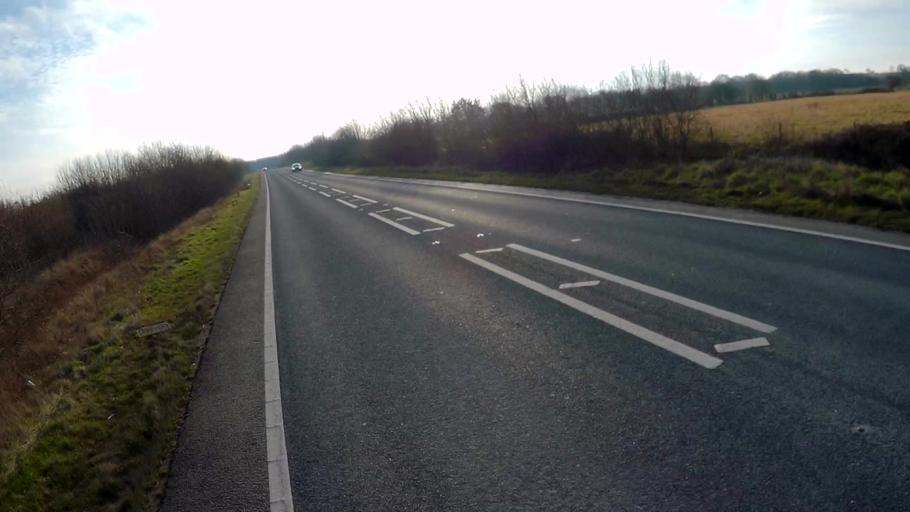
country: GB
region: England
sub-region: Lincolnshire
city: Bourne
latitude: 52.7617
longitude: -0.3948
